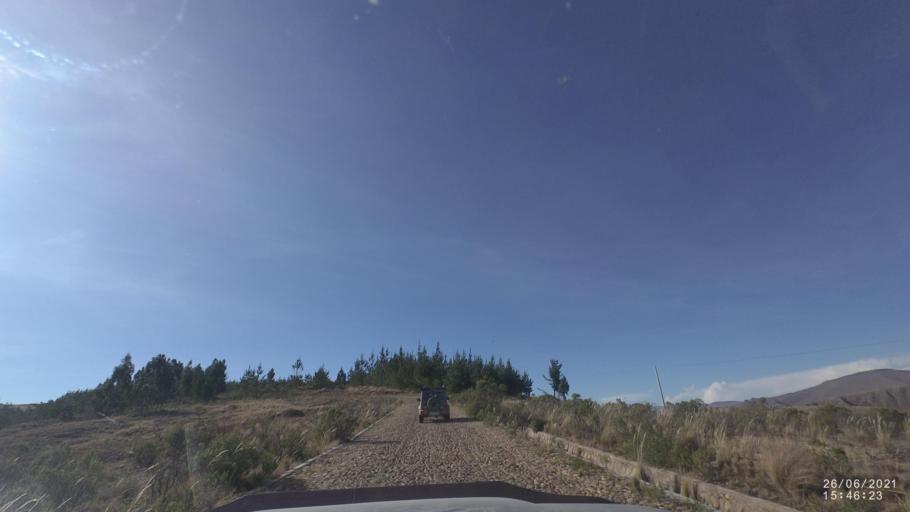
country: BO
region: Cochabamba
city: Arani
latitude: -17.8762
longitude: -65.6990
